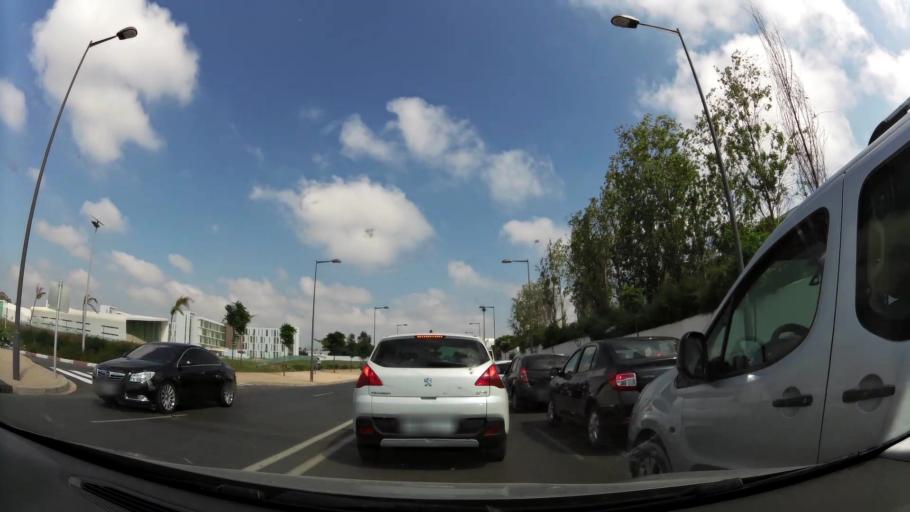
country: MA
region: Rabat-Sale-Zemmour-Zaer
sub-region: Rabat
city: Rabat
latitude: 33.9725
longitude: -6.8702
